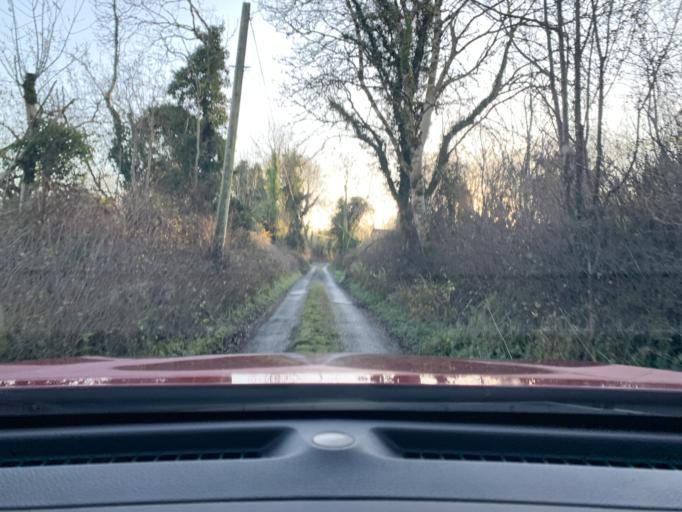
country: IE
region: Connaught
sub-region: Sligo
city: Ballymote
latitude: 53.9845
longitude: -8.5148
